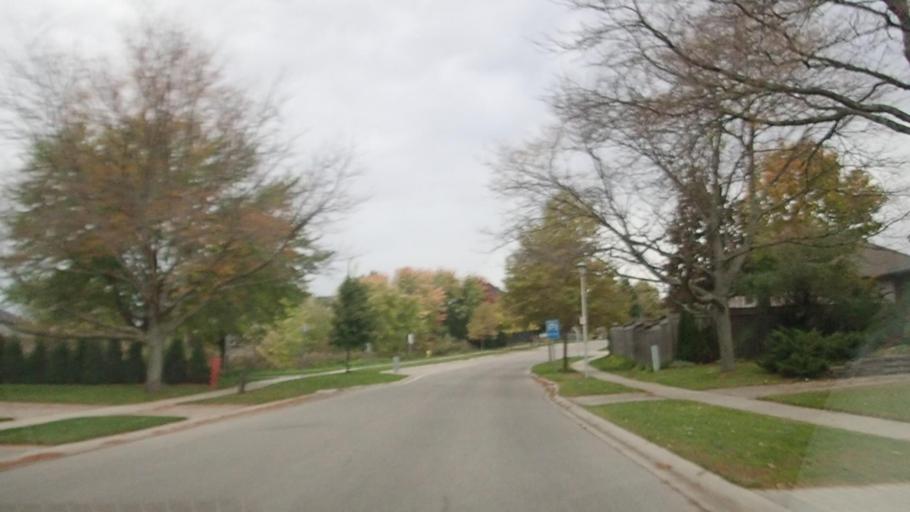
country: CA
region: Ontario
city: London
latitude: 43.0379
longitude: -81.2664
